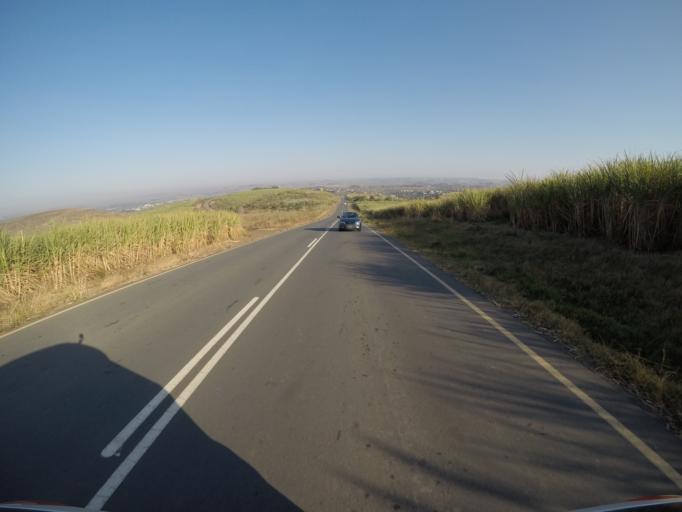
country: ZA
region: KwaZulu-Natal
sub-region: iLembe District Municipality
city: Stanger
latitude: -29.4266
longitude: 31.2681
